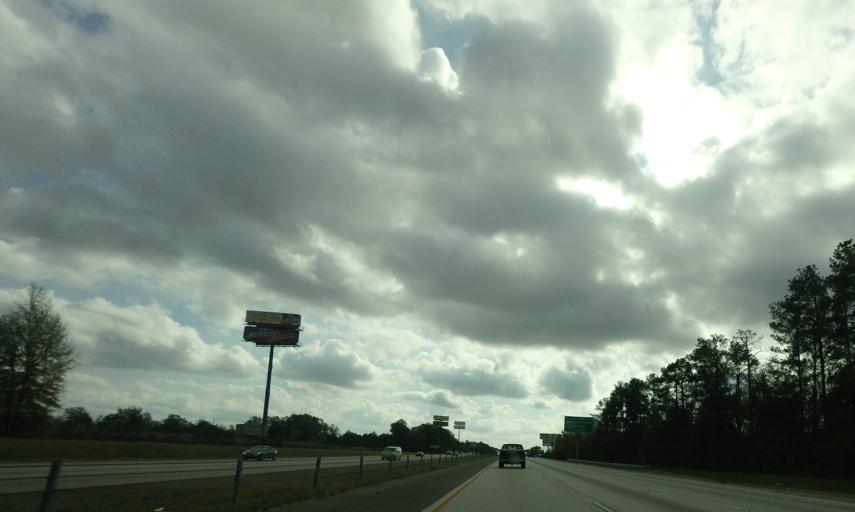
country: US
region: Georgia
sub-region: Peach County
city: Byron
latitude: 32.6073
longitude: -83.7427
